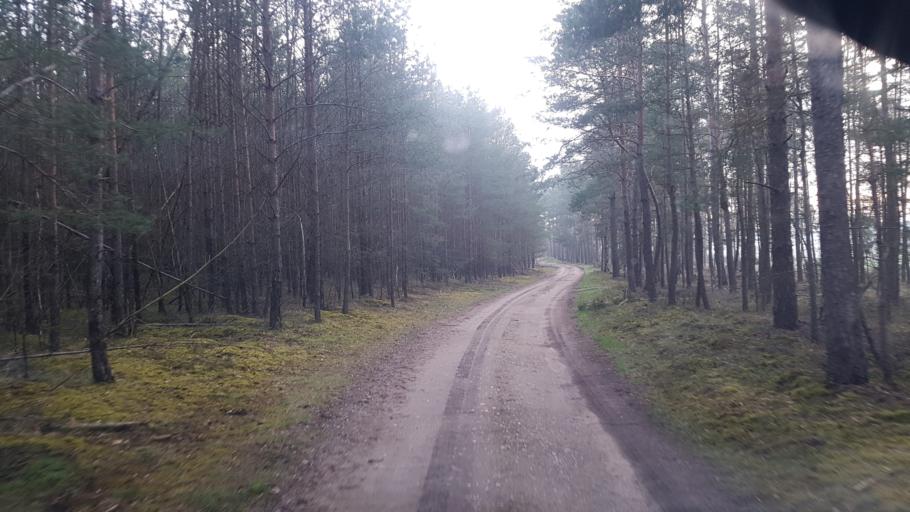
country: DE
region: Brandenburg
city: Trobitz
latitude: 51.5488
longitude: 13.4588
